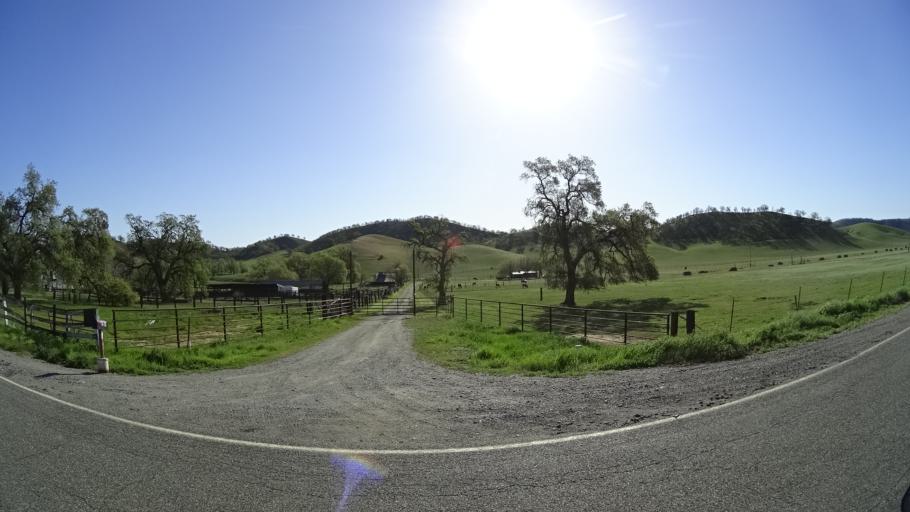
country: US
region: California
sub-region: Tehama County
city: Rancho Tehama Reserve
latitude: 39.7722
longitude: -122.5221
